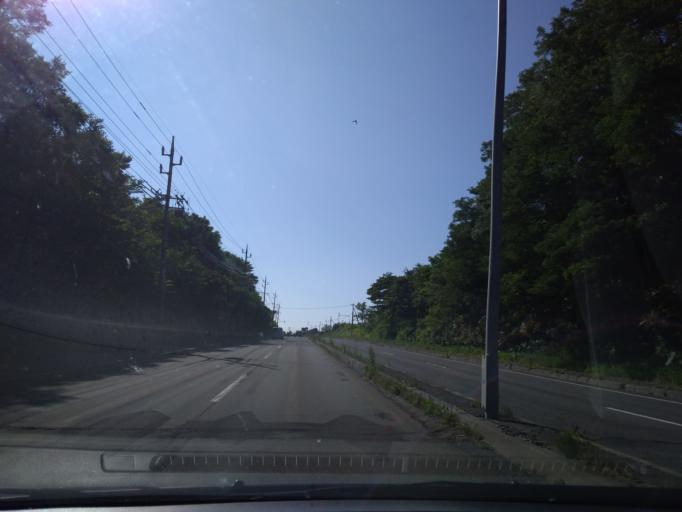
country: JP
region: Hokkaido
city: Kitahiroshima
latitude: 42.9792
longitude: 141.5048
